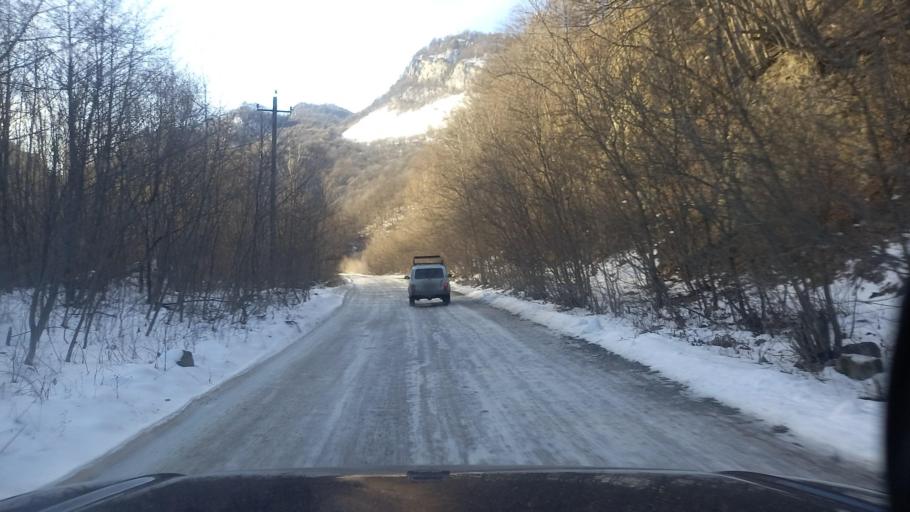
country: RU
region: North Ossetia
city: Gizel'
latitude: 42.9151
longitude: 44.5358
